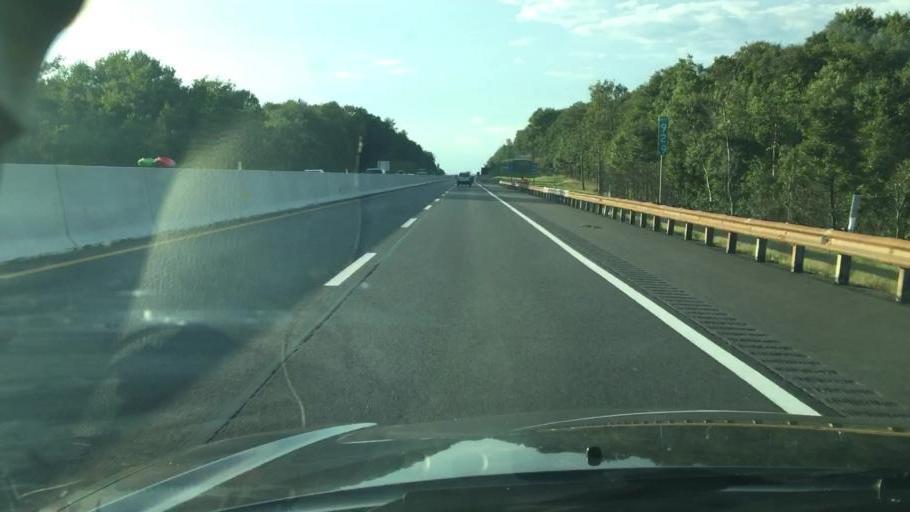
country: US
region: Pennsylvania
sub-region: Luzerne County
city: White Haven
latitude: 41.0562
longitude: -75.6809
